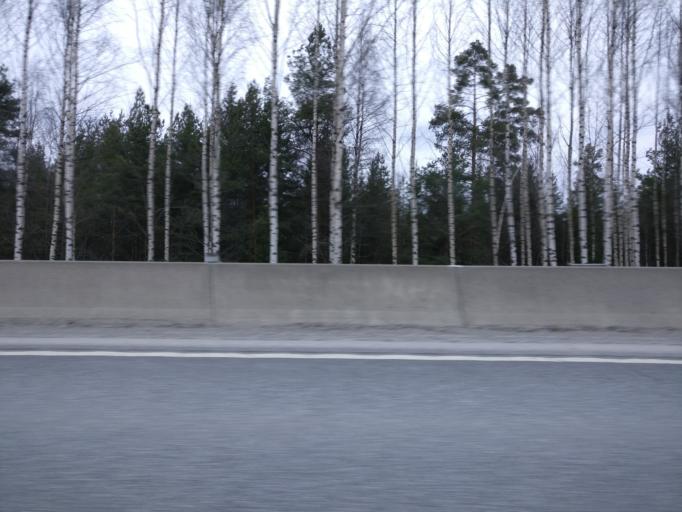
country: FI
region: Pirkanmaa
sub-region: Tampere
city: Tampere
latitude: 61.4666
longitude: 23.8149
